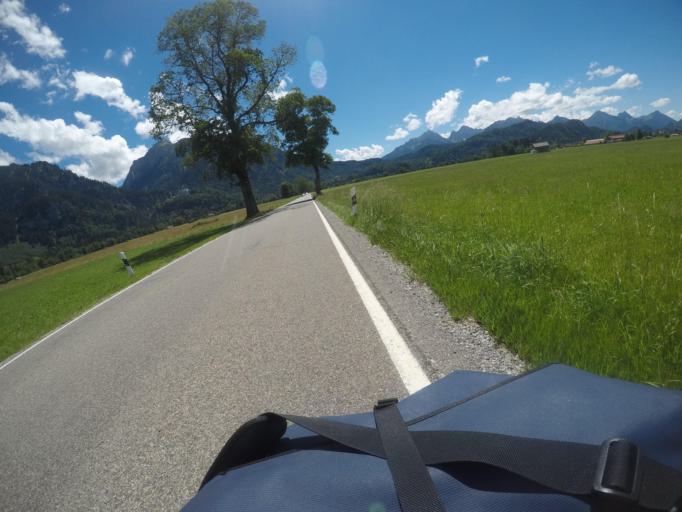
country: DE
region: Bavaria
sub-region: Swabia
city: Schwangau
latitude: 47.5730
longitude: 10.7464
